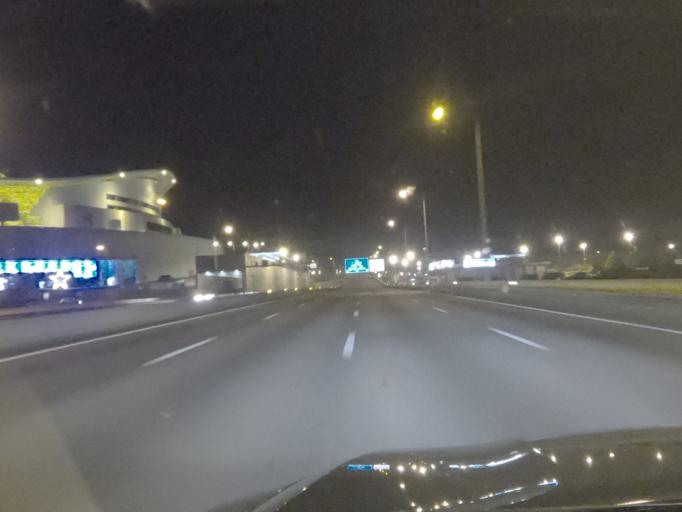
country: PT
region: Porto
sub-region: Porto
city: Porto
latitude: 41.1588
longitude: -8.5824
